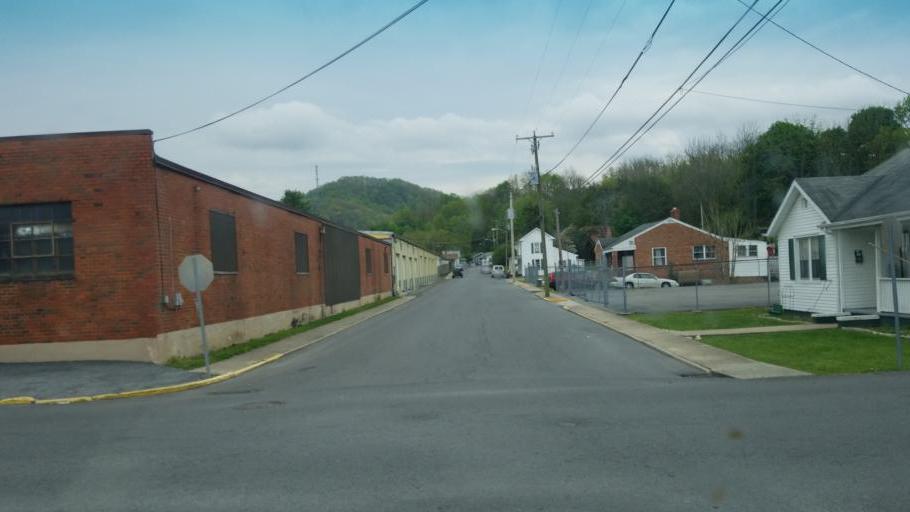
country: US
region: Virginia
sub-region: Smyth County
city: Marion
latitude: 36.8323
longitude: -81.5165
